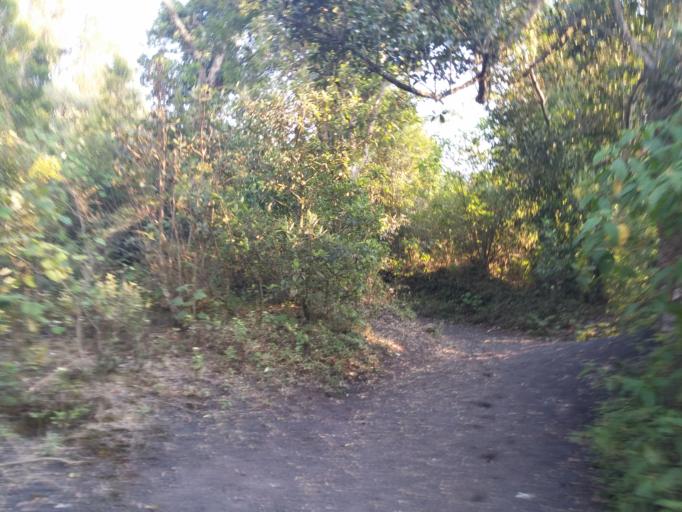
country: GT
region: Escuintla
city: San Vicente Pacaya
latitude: 14.3934
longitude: -90.6003
